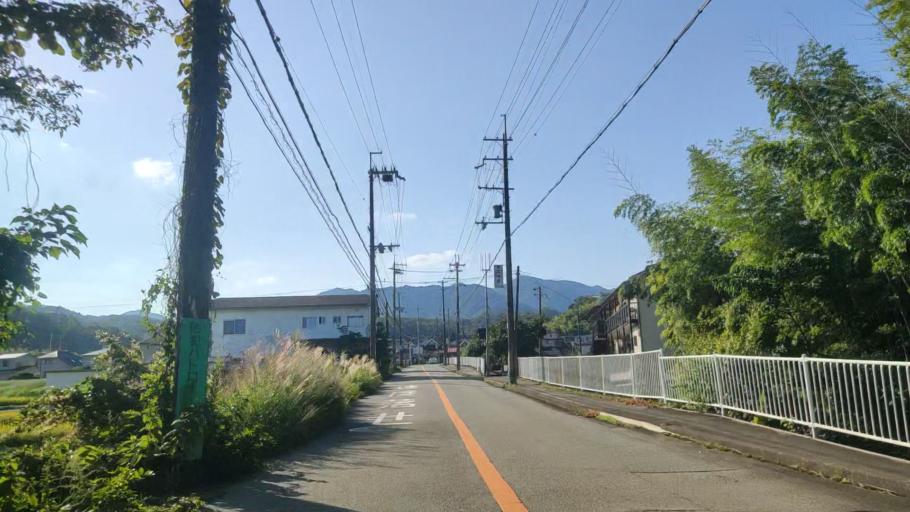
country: JP
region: Hyogo
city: Sandacho
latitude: 34.8131
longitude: 135.2491
